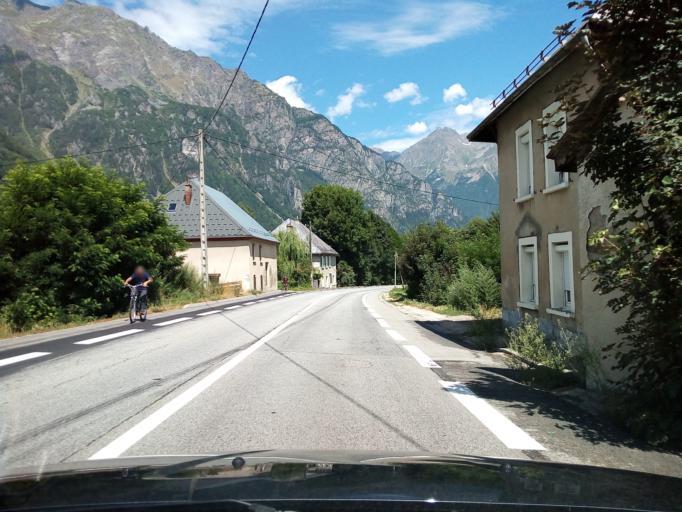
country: FR
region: Rhone-Alpes
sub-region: Departement de l'Isere
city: Huez
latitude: 45.0757
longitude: 6.0153
